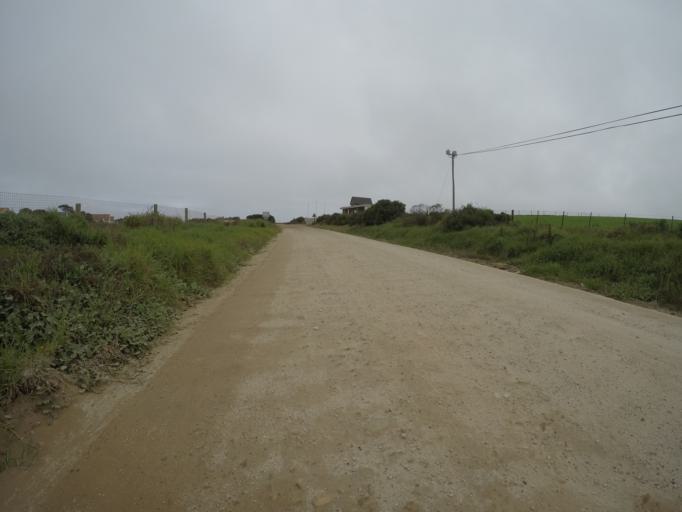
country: ZA
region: Eastern Cape
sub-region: Cacadu District Municipality
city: Kareedouw
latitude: -34.0704
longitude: 24.2353
